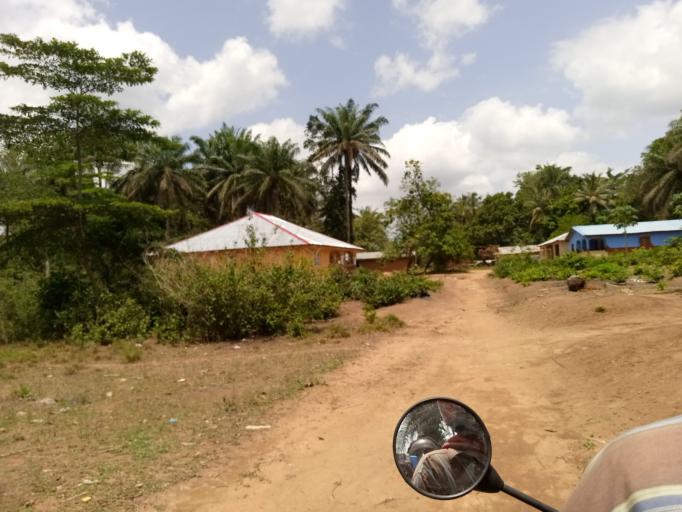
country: SL
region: Western Area
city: Waterloo
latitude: 8.4035
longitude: -13.0247
